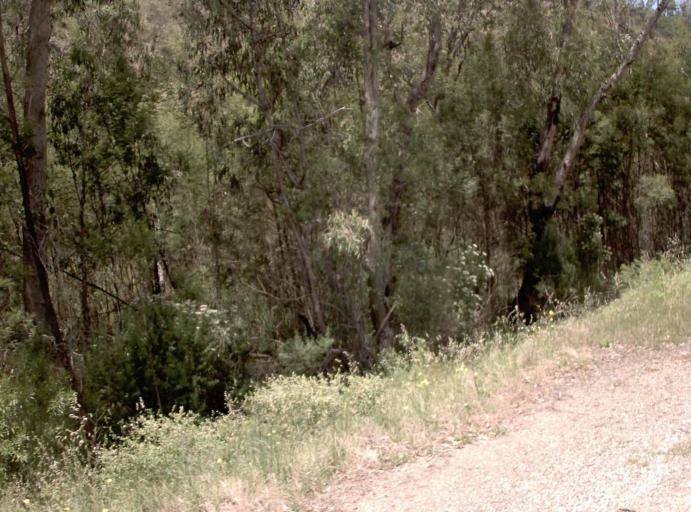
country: AU
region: Victoria
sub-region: East Gippsland
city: Lakes Entrance
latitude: -37.5216
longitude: 147.8484
